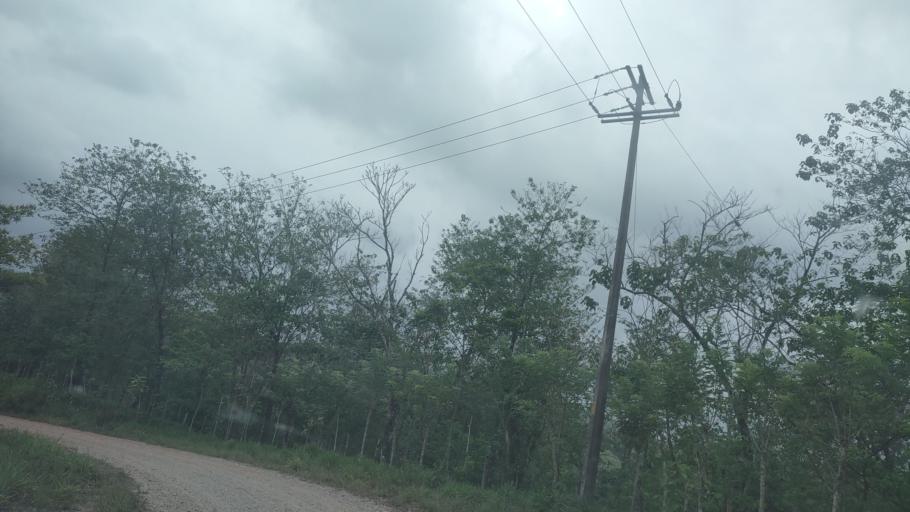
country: MX
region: Tabasco
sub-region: Huimanguillo
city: Francisco Rueda
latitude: 17.4390
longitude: -94.0291
